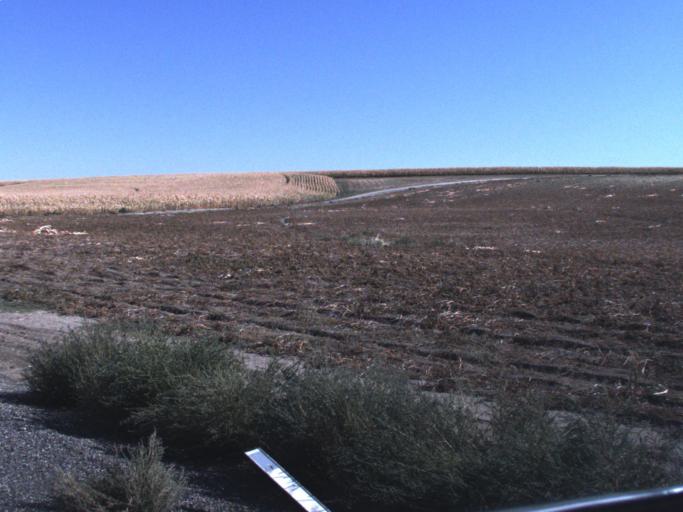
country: US
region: Washington
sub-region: Walla Walla County
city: Burbank
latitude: 46.2492
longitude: -118.8123
